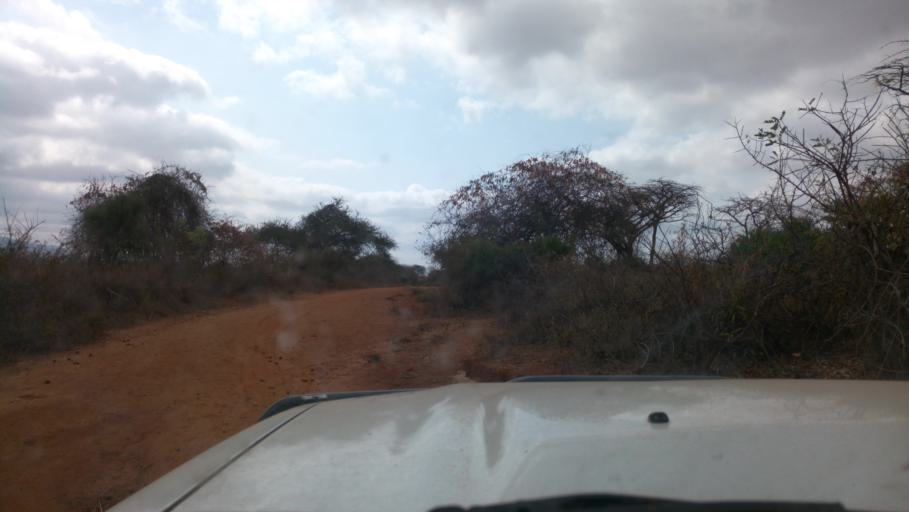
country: KE
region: Kitui
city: Kitui
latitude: -1.8317
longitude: 38.3162
